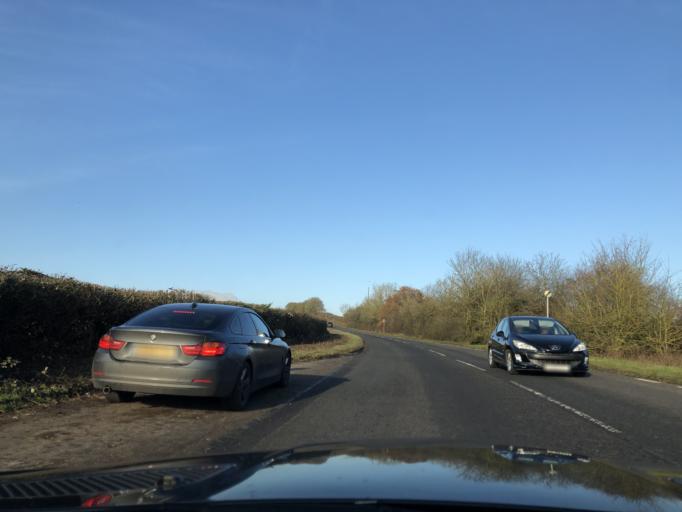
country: GB
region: England
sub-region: Buckinghamshire
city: Marlow
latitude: 51.5945
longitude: -0.7664
